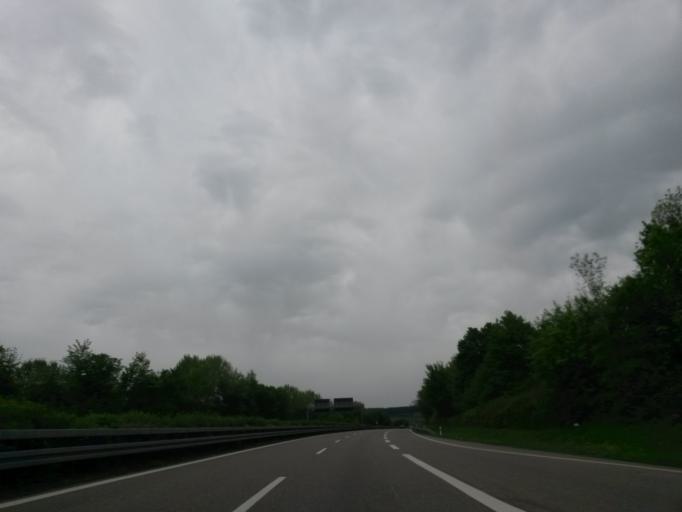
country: DE
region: Baden-Wuerttemberg
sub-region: Regierungsbezirk Stuttgart
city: Weinsberg
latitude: 49.1606
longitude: 9.3005
